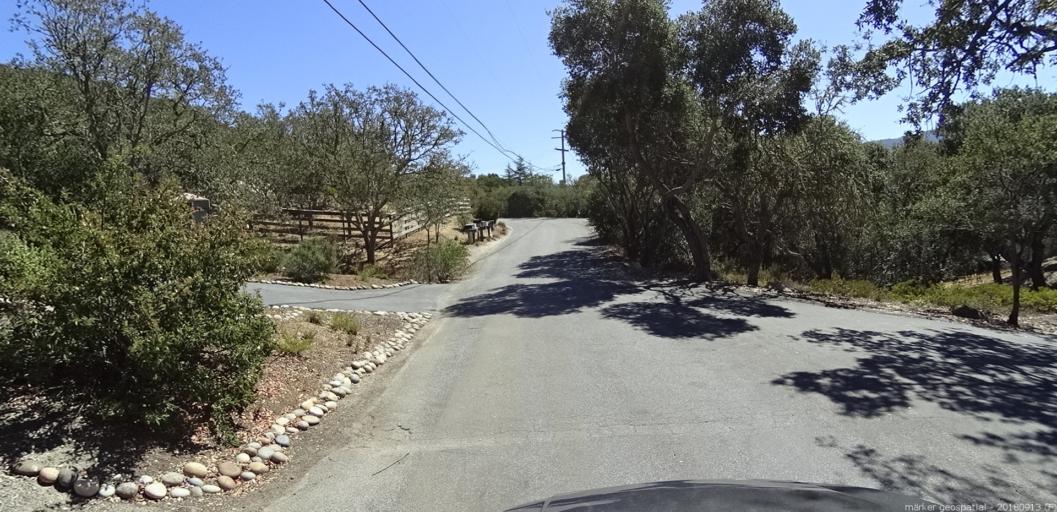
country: US
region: California
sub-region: Monterey County
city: Carmel Valley Village
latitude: 36.5121
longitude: -121.7578
